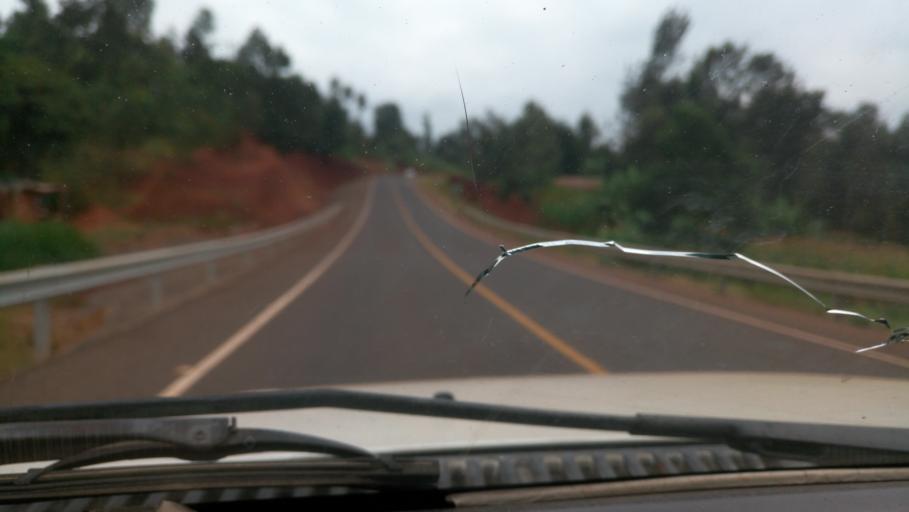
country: KE
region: Murang'a District
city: Kangema
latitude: -0.7840
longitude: 36.9886
